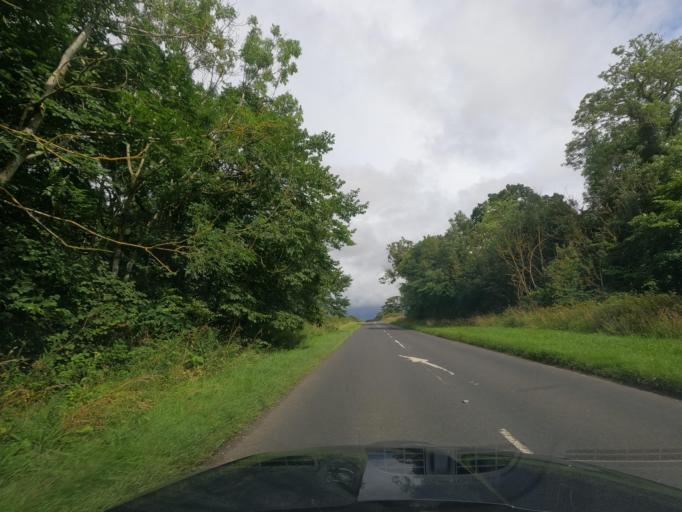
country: GB
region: England
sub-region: Northumberland
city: Ancroft
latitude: 55.6828
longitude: -2.0025
